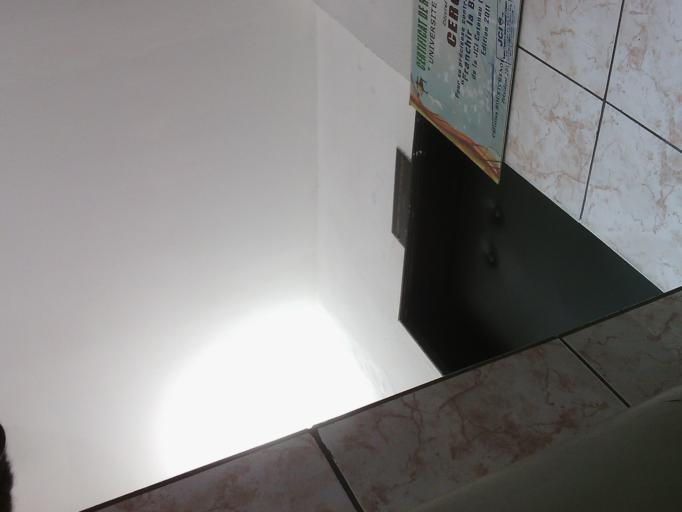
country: BJ
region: Littoral
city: Cotonou
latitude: 6.3696
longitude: 2.4160
